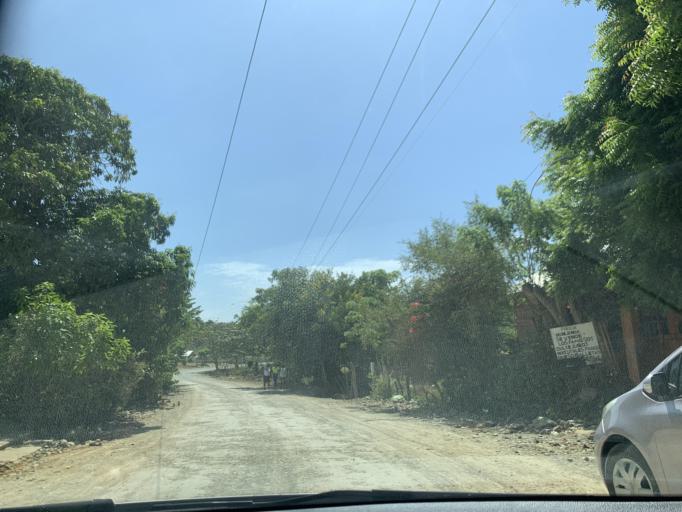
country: DO
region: Puerto Plata
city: Luperon
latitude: 19.8817
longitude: -70.8415
